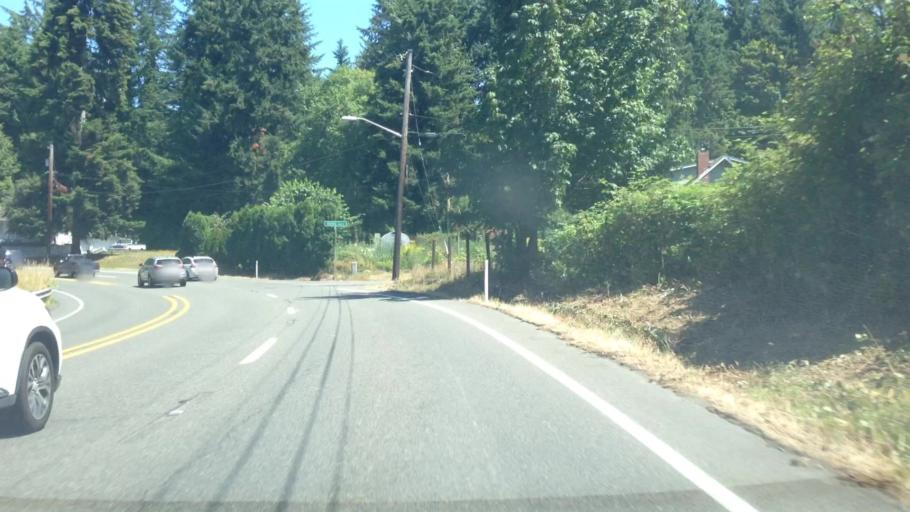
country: US
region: Washington
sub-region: Pierce County
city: North Puyallup
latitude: 47.2211
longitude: -122.2947
